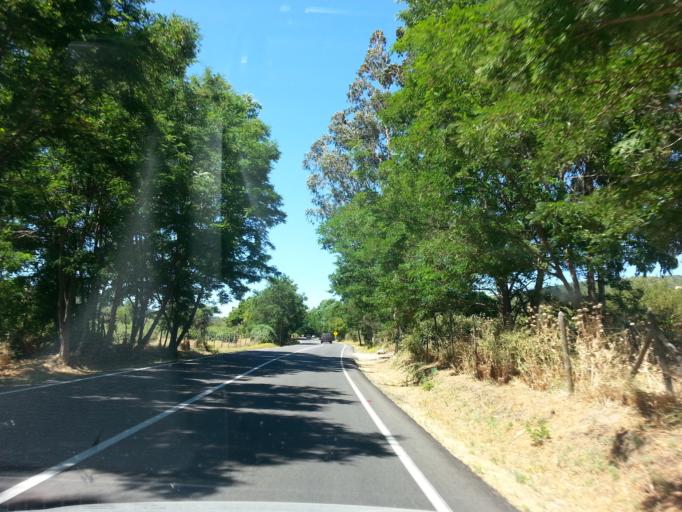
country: CL
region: Valparaiso
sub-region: Provincia de Marga Marga
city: Villa Alemana
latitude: -33.2058
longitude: -71.3838
